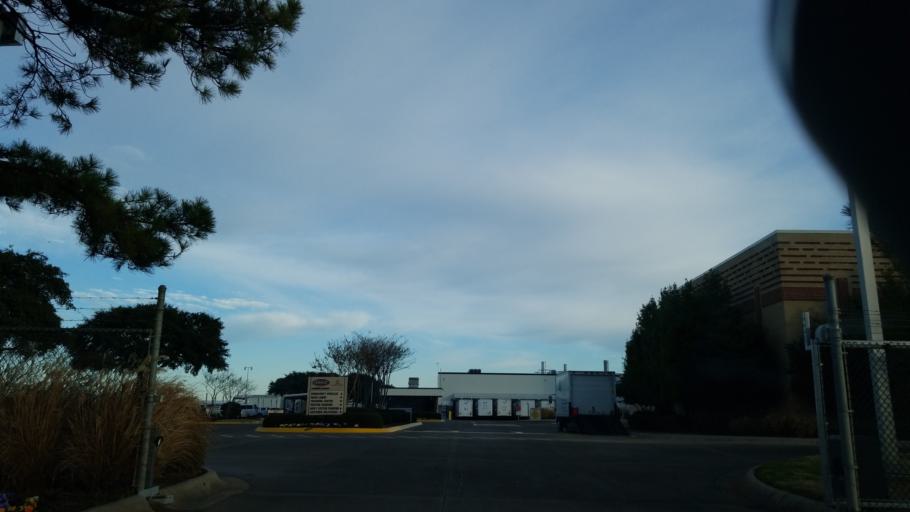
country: US
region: Texas
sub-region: Denton County
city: Denton
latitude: 33.2019
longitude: -97.1774
